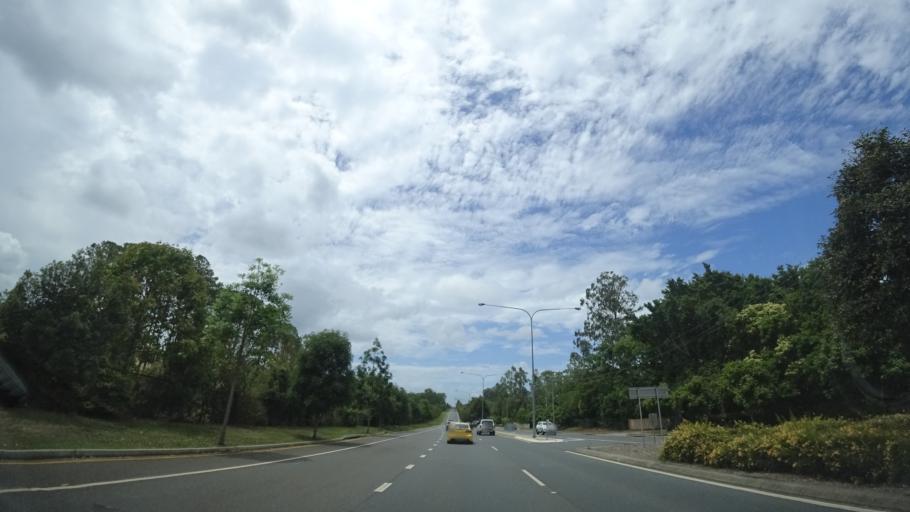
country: AU
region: Queensland
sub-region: Brisbane
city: Bridegman Downs
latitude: -27.3521
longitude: 152.9957
